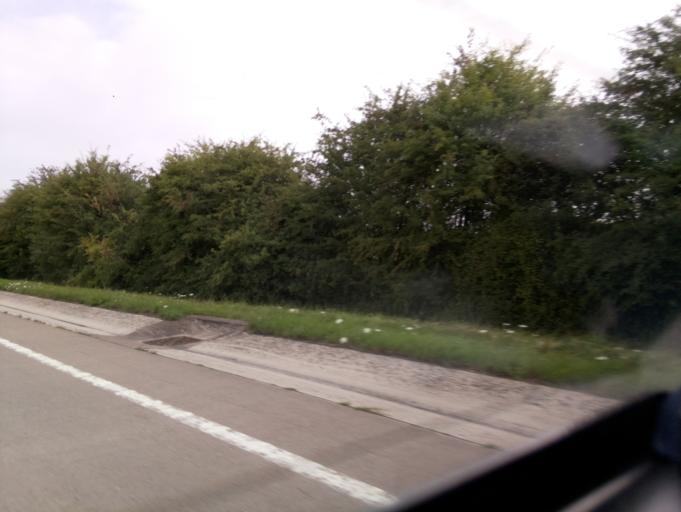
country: GB
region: England
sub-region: Gloucestershire
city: Cirencester
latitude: 51.7139
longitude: -1.9339
